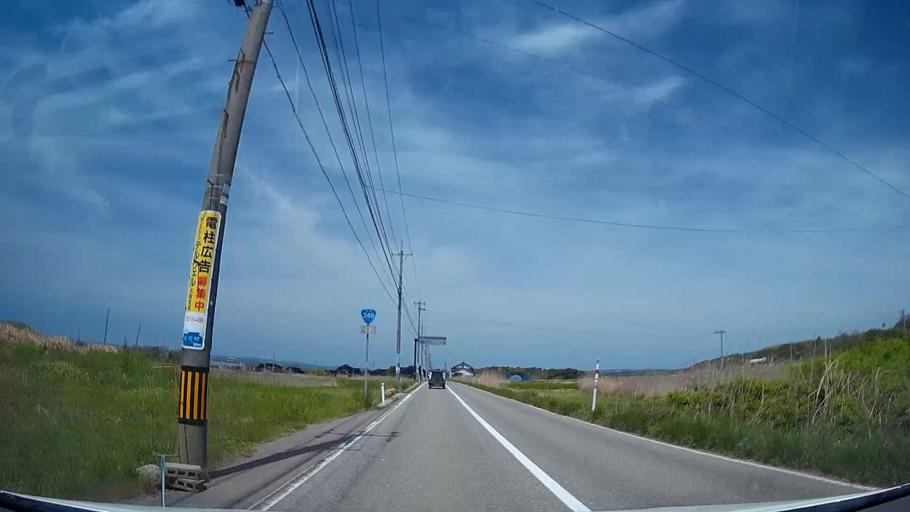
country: JP
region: Ishikawa
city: Hakui
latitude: 36.9403
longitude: 136.7609
